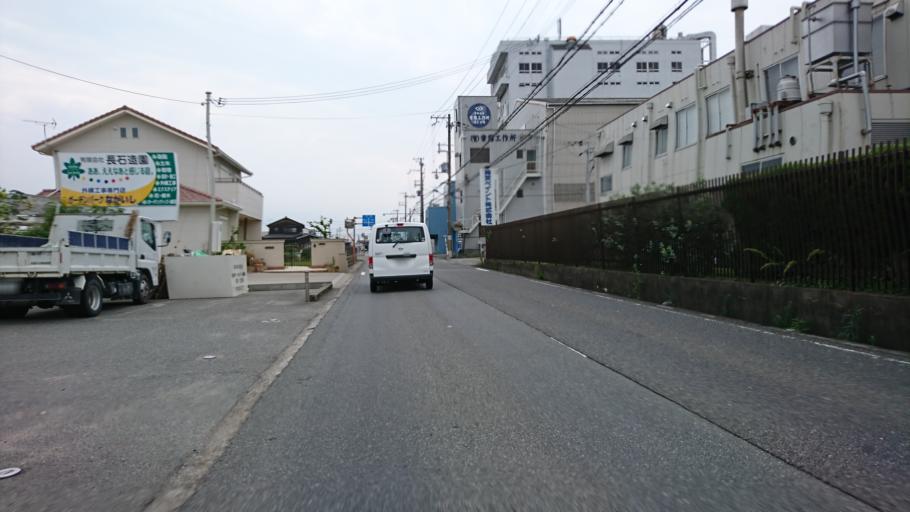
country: JP
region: Hyogo
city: Miki
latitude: 34.7314
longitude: 134.9201
